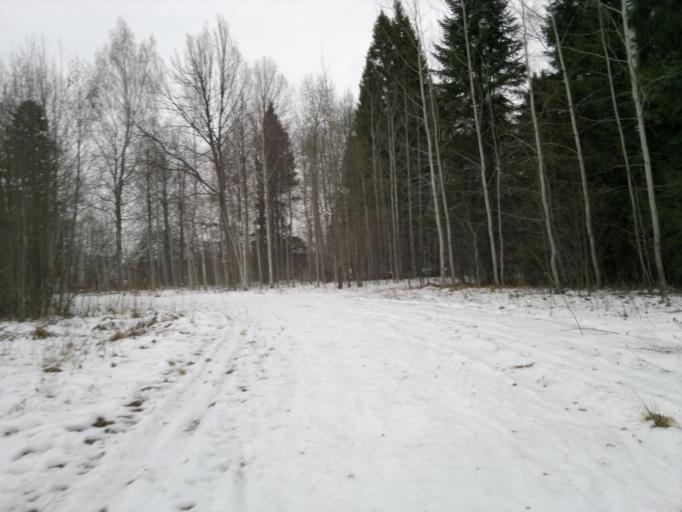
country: RU
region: Mariy-El
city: Yoshkar-Ola
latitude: 56.5962
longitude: 47.9686
